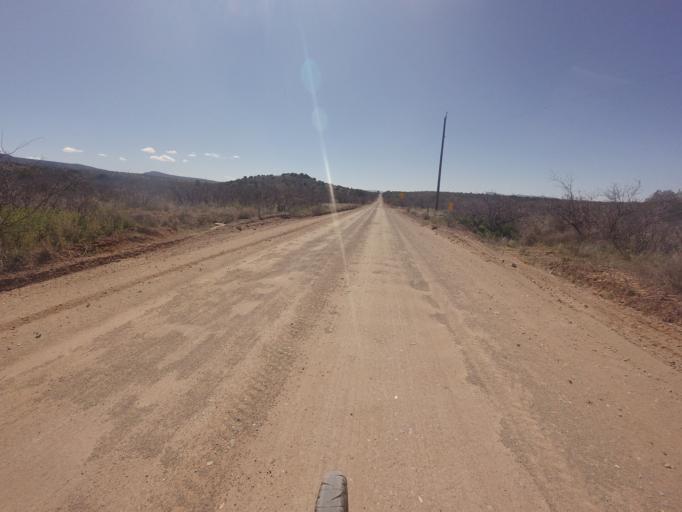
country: US
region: Arizona
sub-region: Yavapai County
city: Lake Montezuma
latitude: 34.6343
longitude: -111.7192
